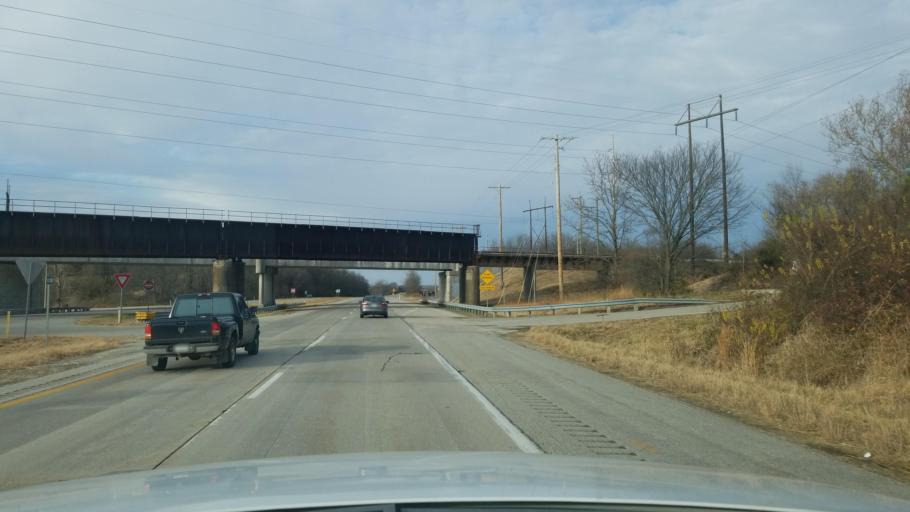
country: US
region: Indiana
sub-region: Posey County
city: Mount Vernon
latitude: 37.9422
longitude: -87.7361
